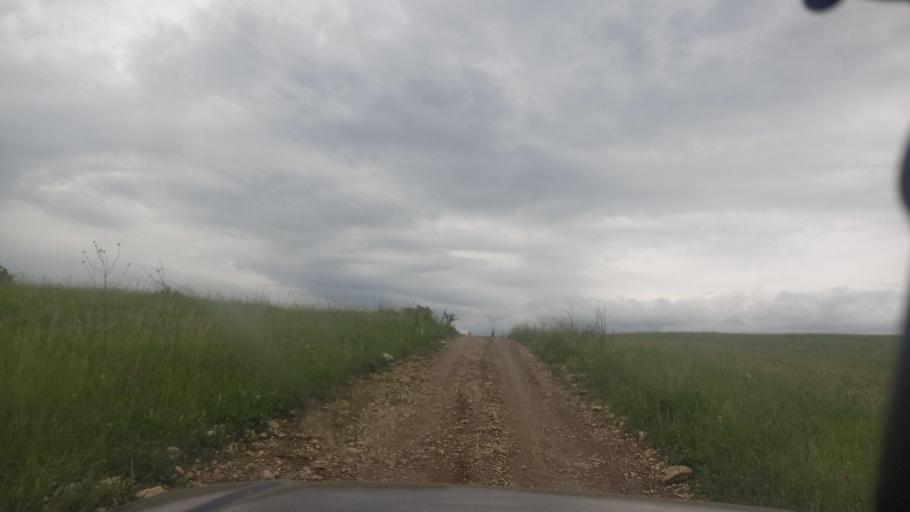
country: RU
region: Krasnodarskiy
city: Peredovaya
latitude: 44.0702
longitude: 41.3628
